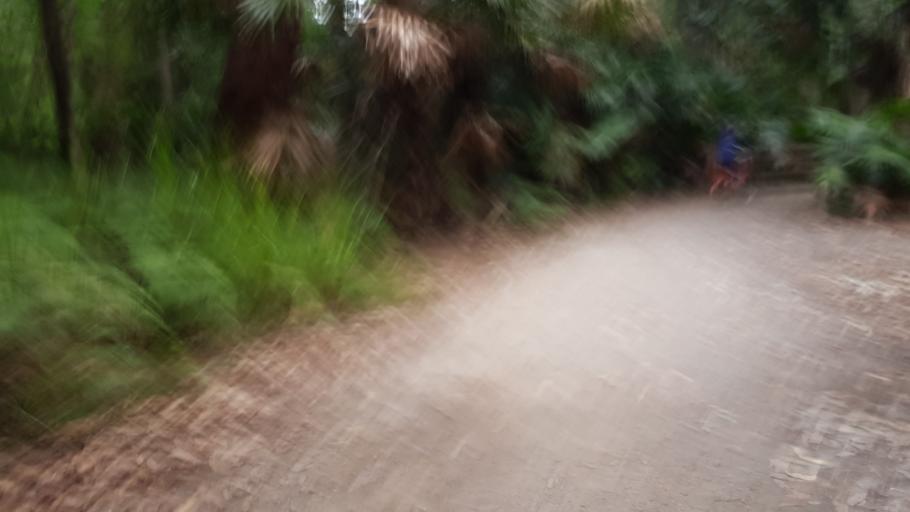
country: AU
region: New South Wales
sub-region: Warringah
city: Narrabeen
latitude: -33.7179
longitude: 151.2808
